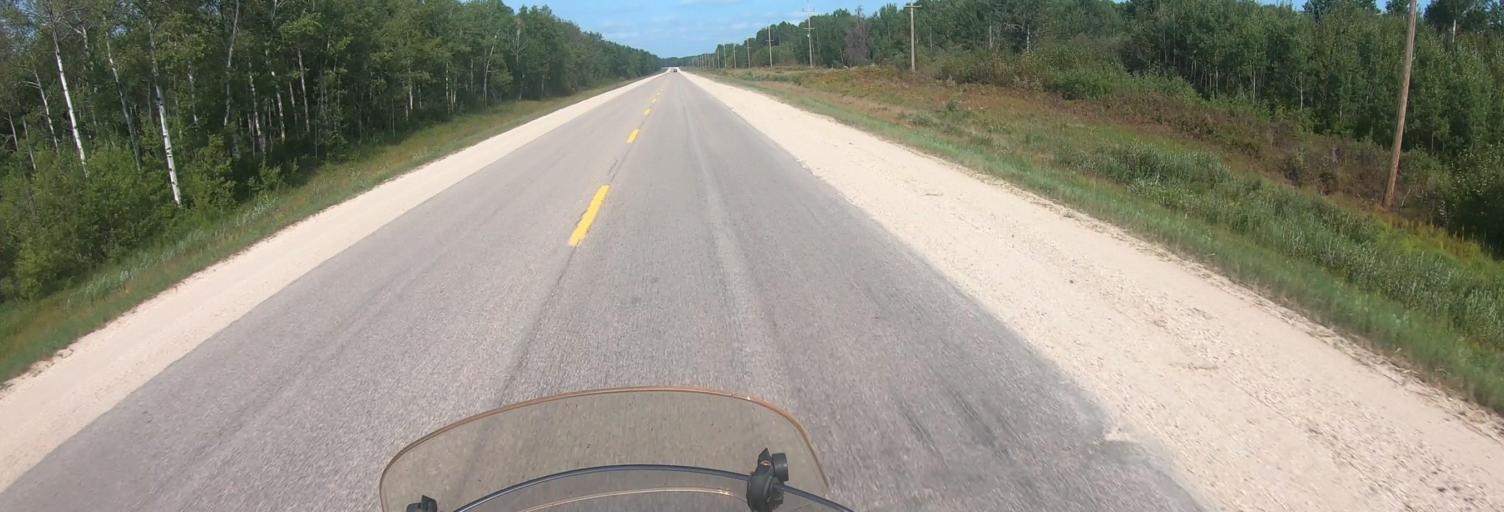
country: CA
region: Manitoba
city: La Broquerie
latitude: 49.1655
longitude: -96.1472
